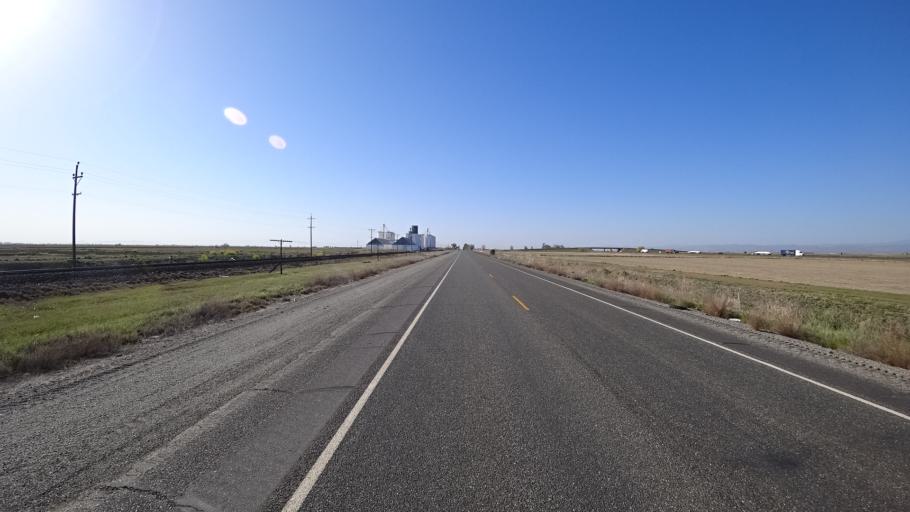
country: US
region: California
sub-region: Glenn County
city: Willows
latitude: 39.4710
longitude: -122.1930
